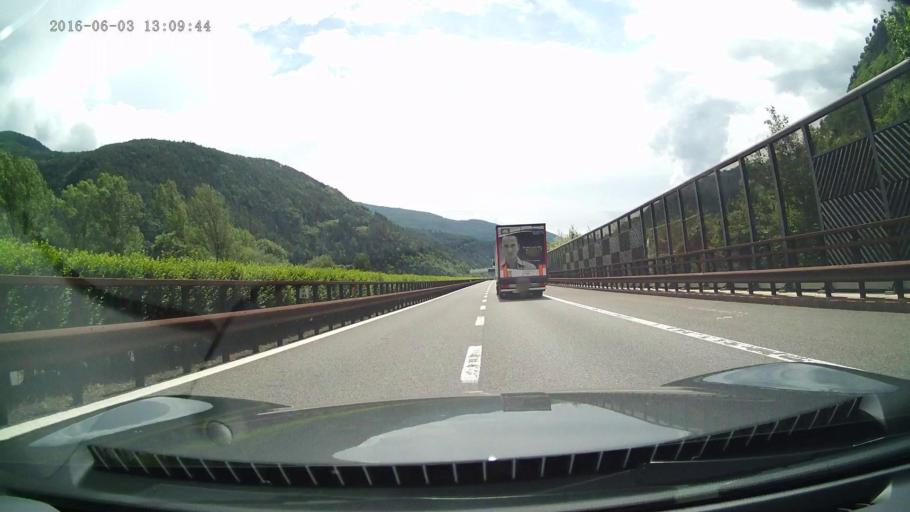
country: IT
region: Trentino-Alto Adige
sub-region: Bolzano
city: Velturno
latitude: 46.6722
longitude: 11.6181
